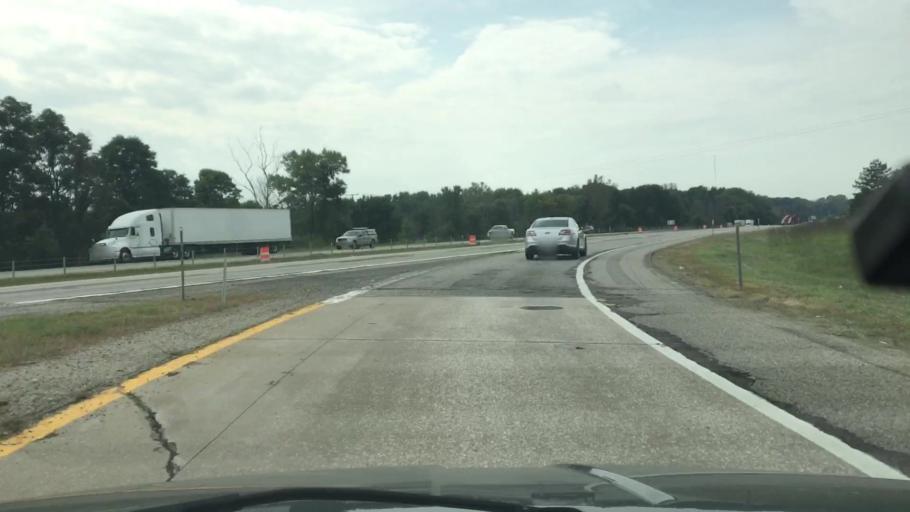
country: US
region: Michigan
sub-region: Berrien County
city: Fair Plain
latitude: 42.0674
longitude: -86.4390
